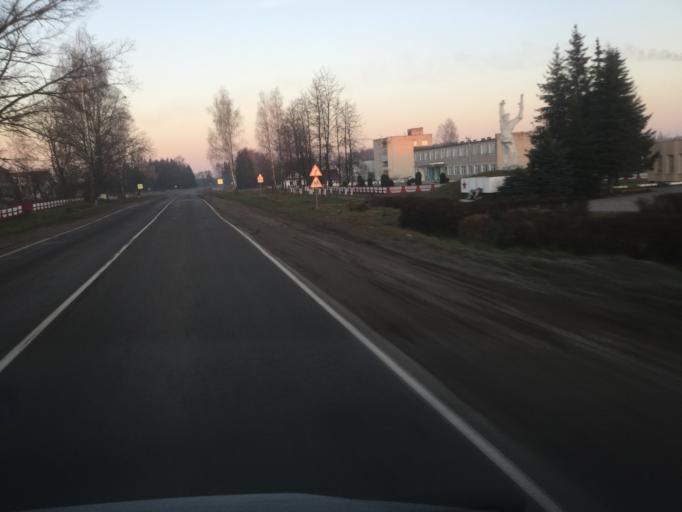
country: BY
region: Vitebsk
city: Vyerkhnyadzvinsk
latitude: 55.7106
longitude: 28.0851
